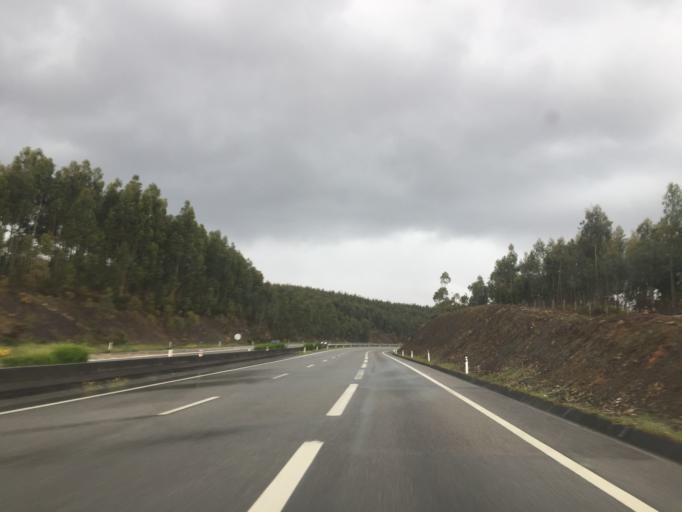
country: PT
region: Aveiro
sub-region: Agueda
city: Valongo
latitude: 40.6609
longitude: -8.3902
